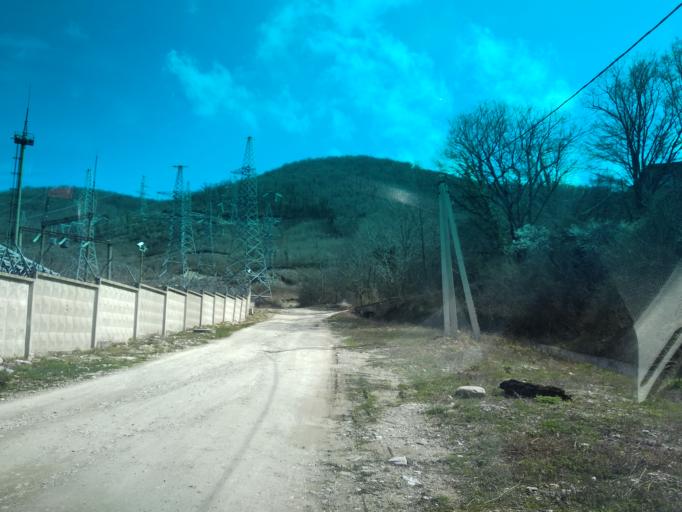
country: RU
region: Krasnodarskiy
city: Shepsi
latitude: 44.0529
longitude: 39.1632
